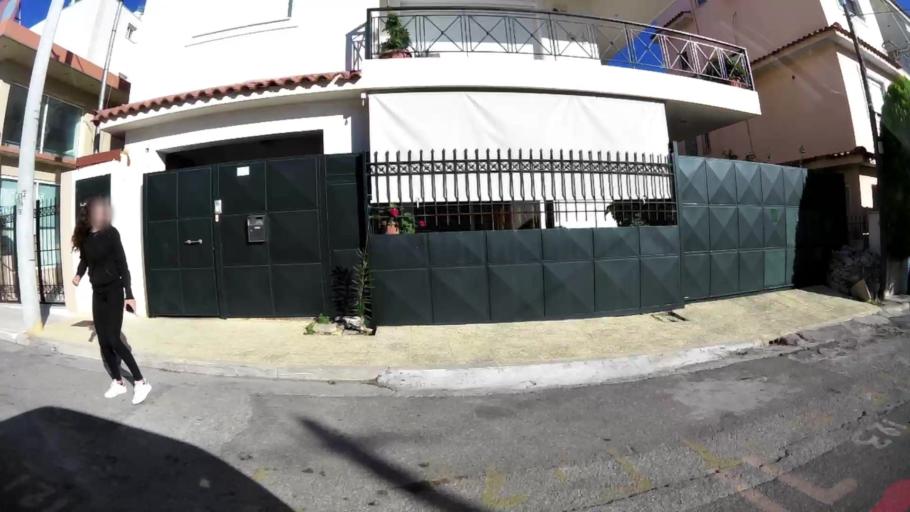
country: GR
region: Attica
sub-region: Nomarchia Anatolikis Attikis
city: Acharnes
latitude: 38.0966
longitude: 23.7281
